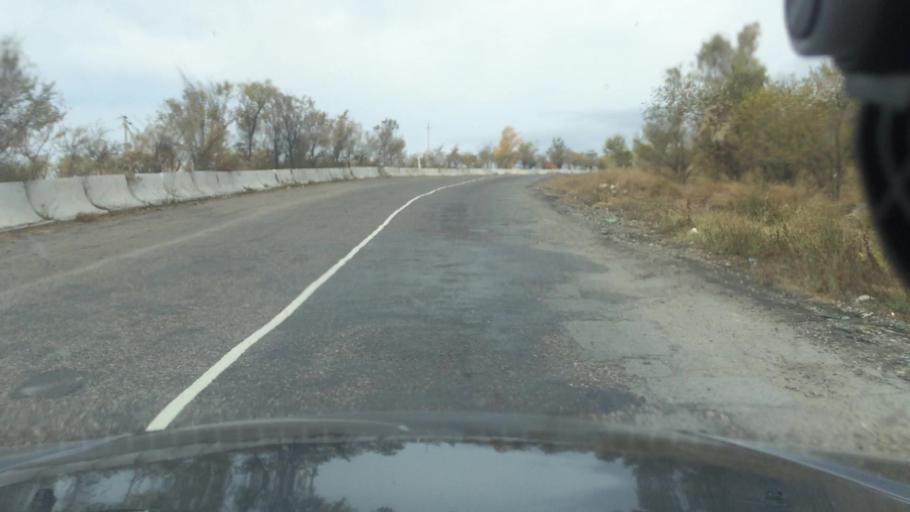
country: KG
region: Ysyk-Koel
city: Karakol
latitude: 42.5970
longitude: 78.3775
